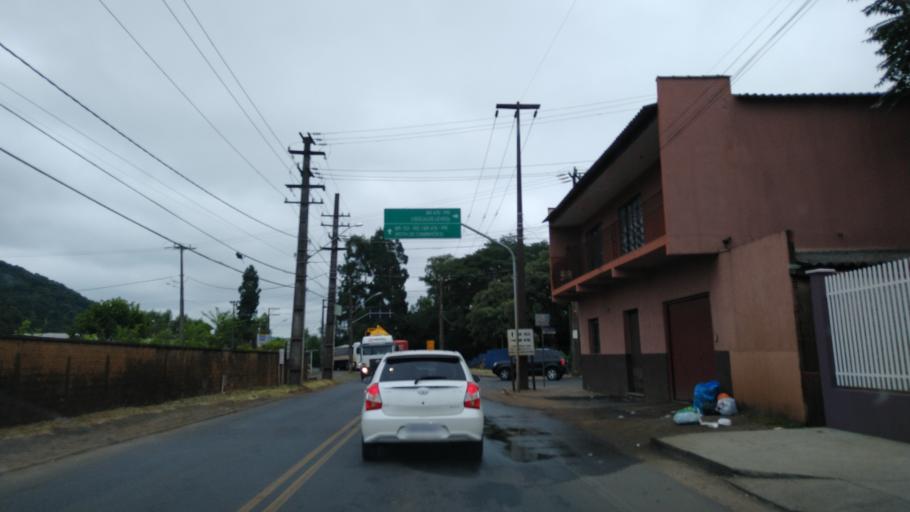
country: BR
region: Parana
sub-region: Uniao Da Vitoria
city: Uniao da Vitoria
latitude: -26.2517
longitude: -51.1002
